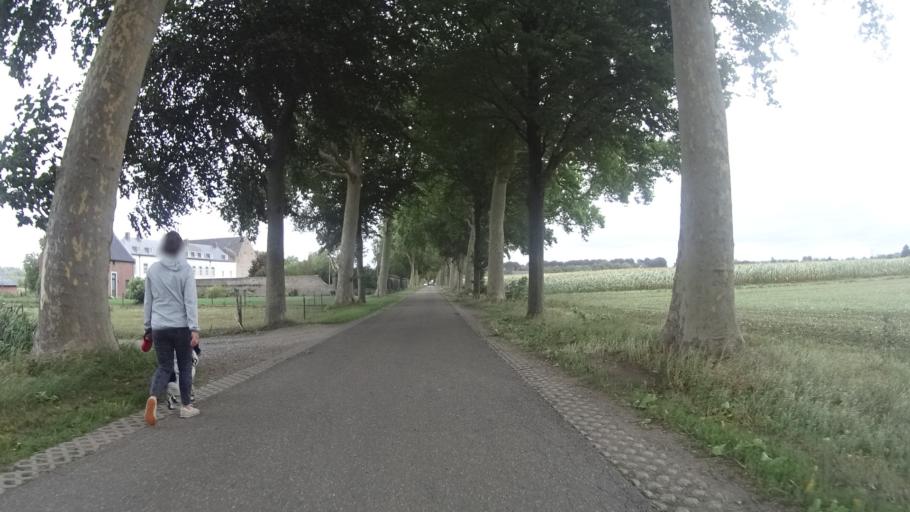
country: NL
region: Limburg
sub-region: Eijsden-Margraten
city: Eijsden
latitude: 50.7668
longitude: 5.6974
